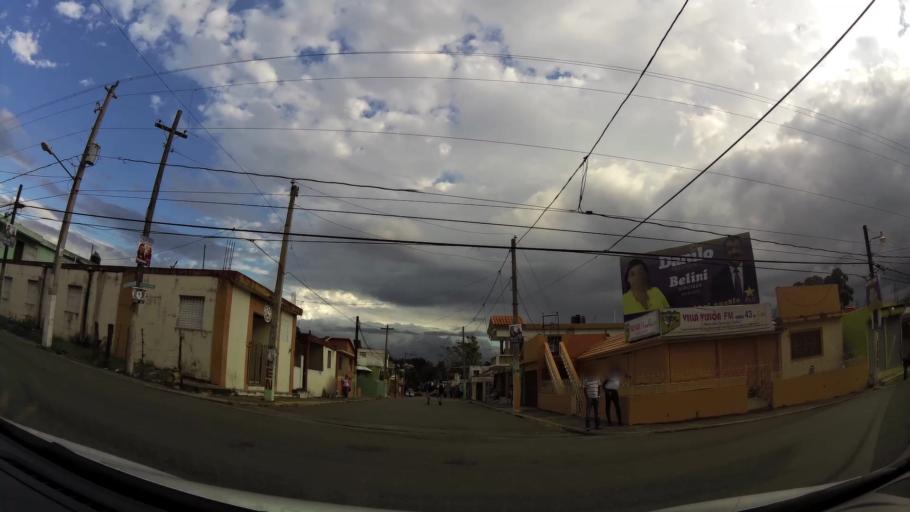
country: DO
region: San Cristobal
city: Villa Altagracia
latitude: 18.6728
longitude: -70.1730
